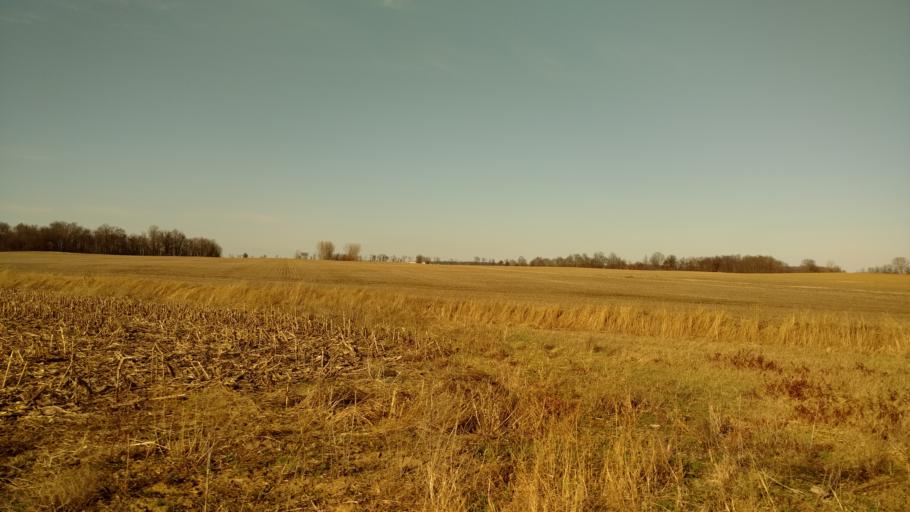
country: US
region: Ohio
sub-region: Crawford County
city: Bucyrus
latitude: 40.7034
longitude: -82.9718
